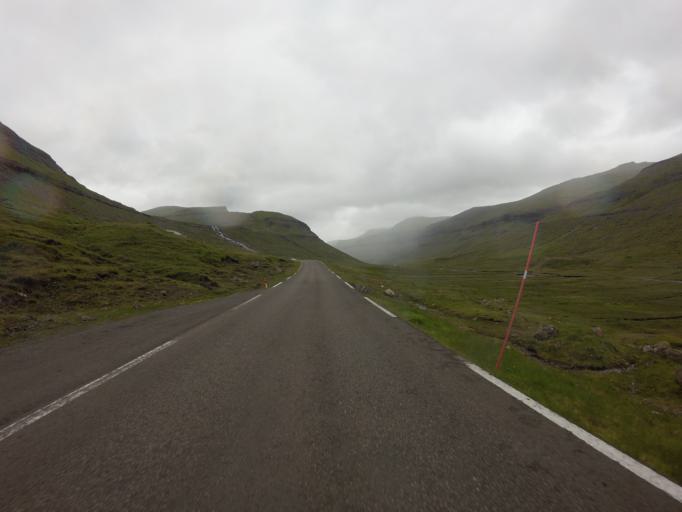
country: FO
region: Streymoy
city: Vestmanna
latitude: 62.2180
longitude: -7.1222
